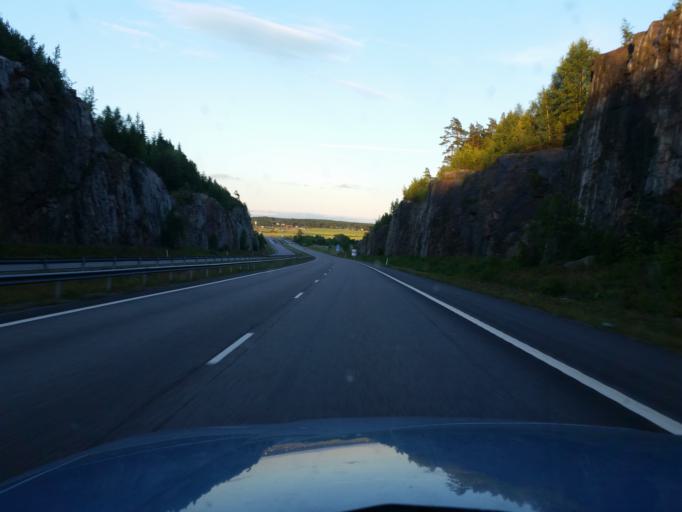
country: FI
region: Varsinais-Suomi
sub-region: Salo
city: Halikko
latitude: 60.4319
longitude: 22.9937
